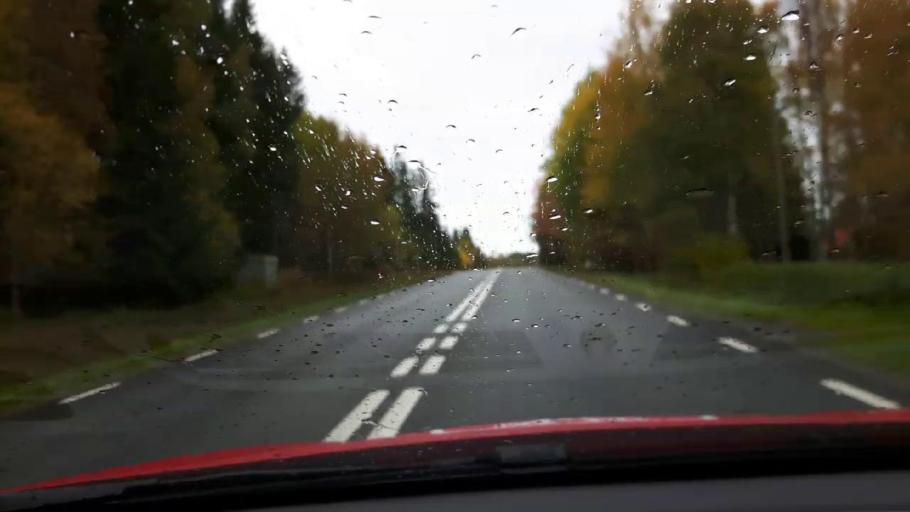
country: SE
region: Jaemtland
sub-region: Krokoms Kommun
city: Krokom
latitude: 63.0995
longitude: 14.3013
